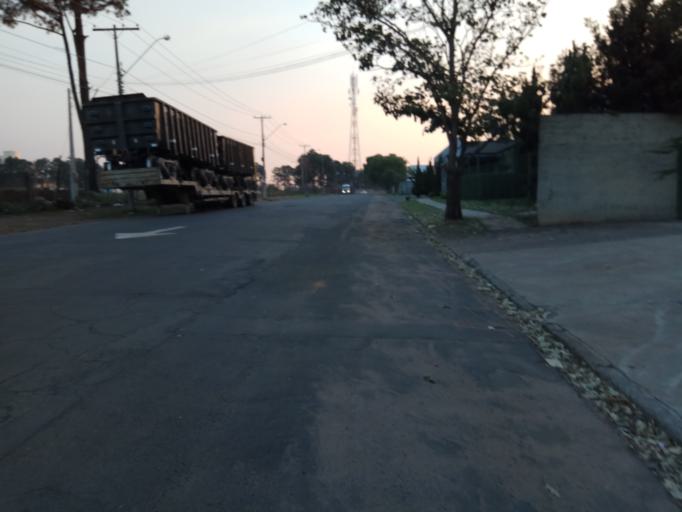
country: BR
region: Sao Paulo
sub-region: Piracicaba
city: Piracicaba
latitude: -22.7350
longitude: -47.5951
